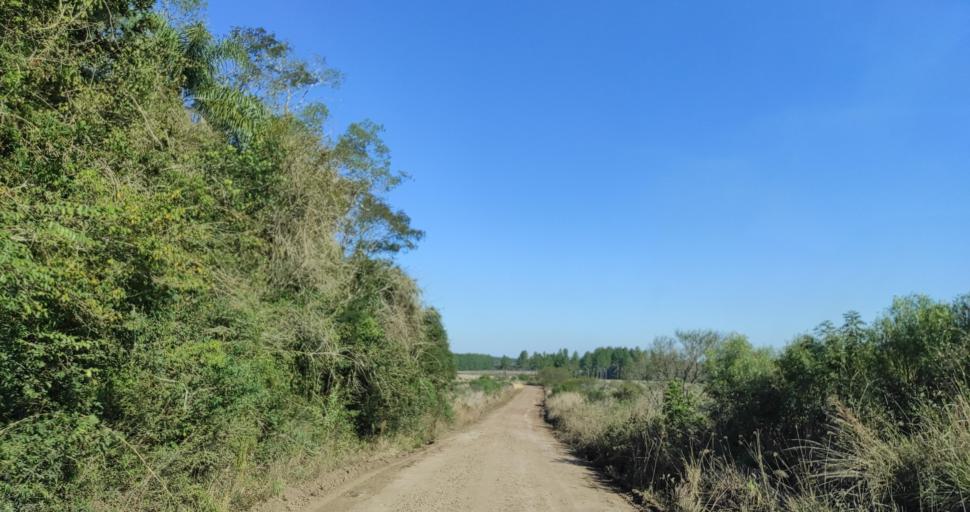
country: AR
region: Misiones
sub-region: Departamento de Apostoles
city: San Jose
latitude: -27.6719
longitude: -55.6612
